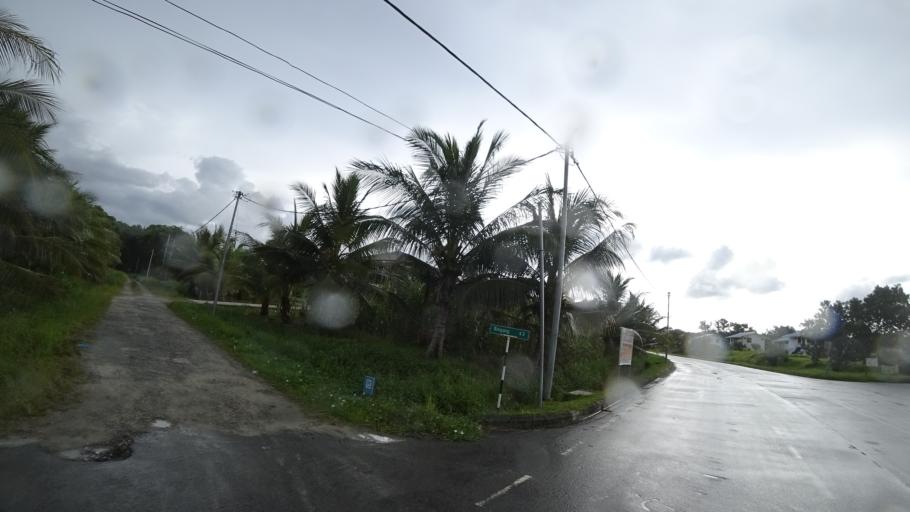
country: BN
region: Brunei and Muara
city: Bandar Seri Begawan
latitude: 4.8360
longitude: 114.9128
